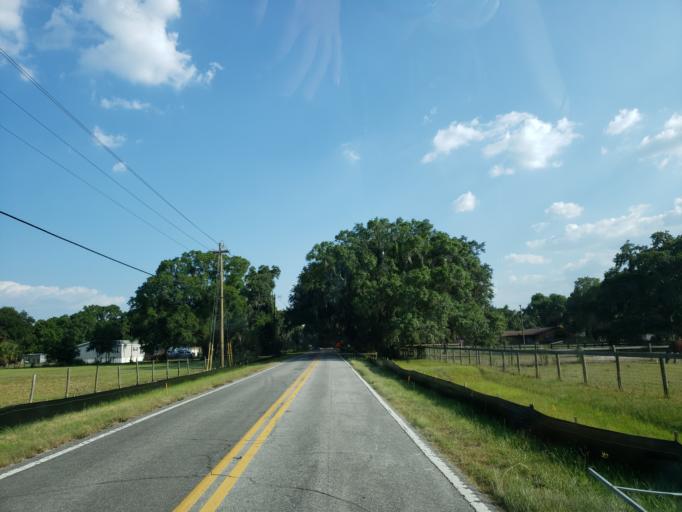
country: US
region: Florida
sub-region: Hillsborough County
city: Fish Hawk
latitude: 27.8459
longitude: -82.2000
